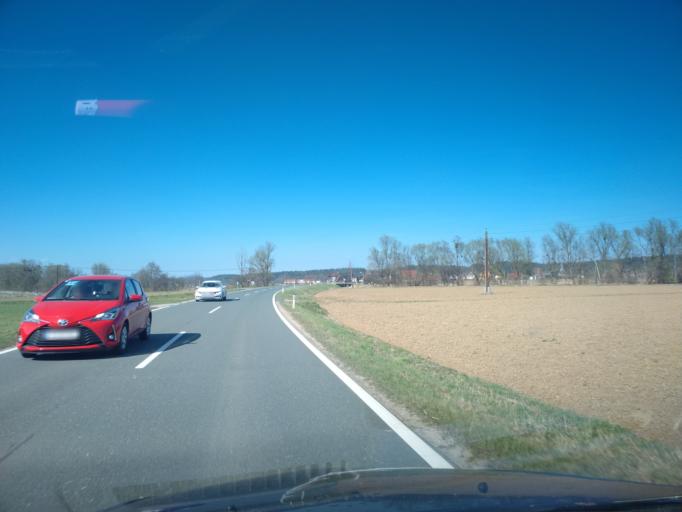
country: AT
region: Styria
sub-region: Politischer Bezirk Deutschlandsberg
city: Preding
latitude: 46.9018
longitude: 15.4076
